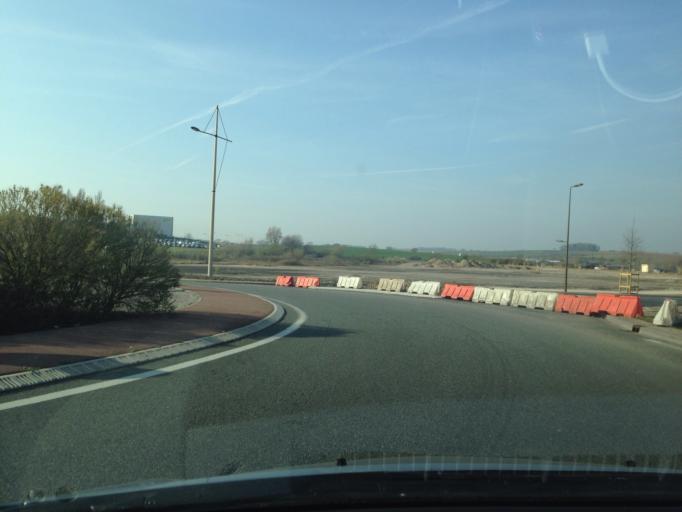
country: FR
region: Nord-Pas-de-Calais
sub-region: Departement du Pas-de-Calais
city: Etaples
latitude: 50.5072
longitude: 1.6657
